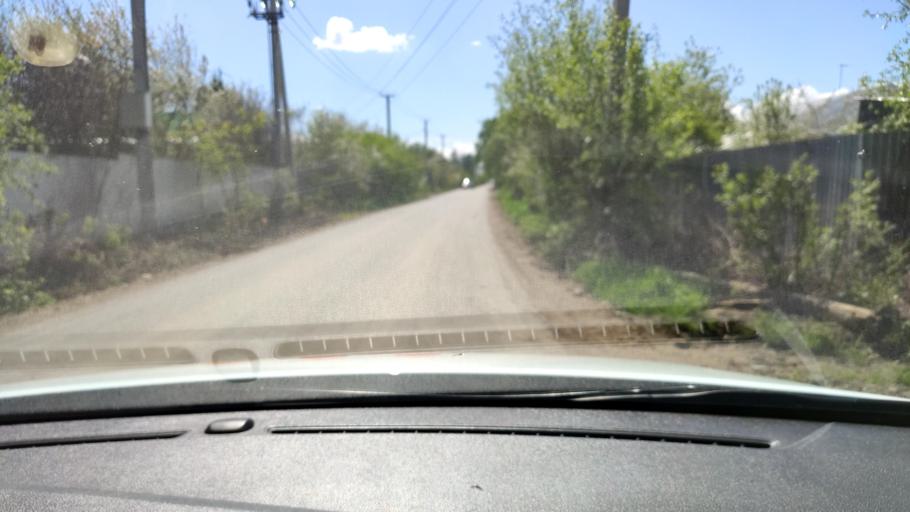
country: RU
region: Tatarstan
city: Vysokaya Gora
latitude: 55.8158
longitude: 49.2809
